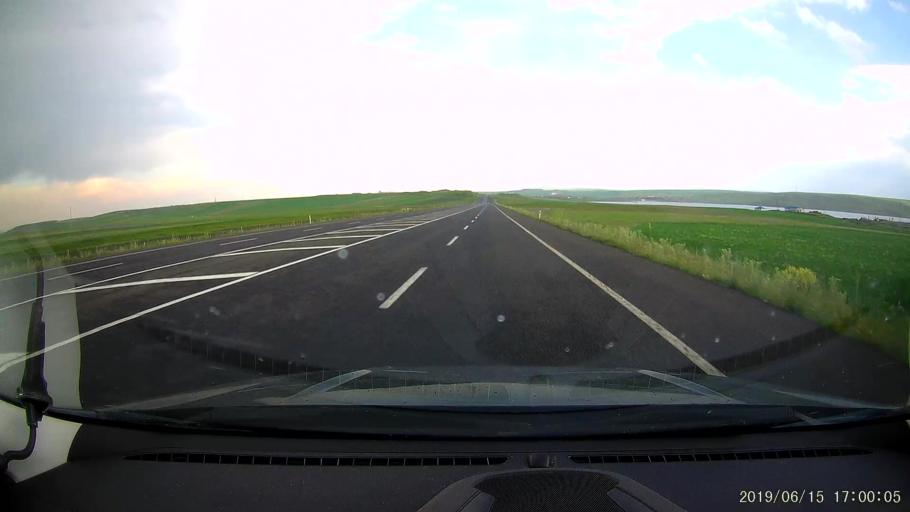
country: TR
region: Kars
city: Susuz
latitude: 40.7432
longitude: 43.1573
